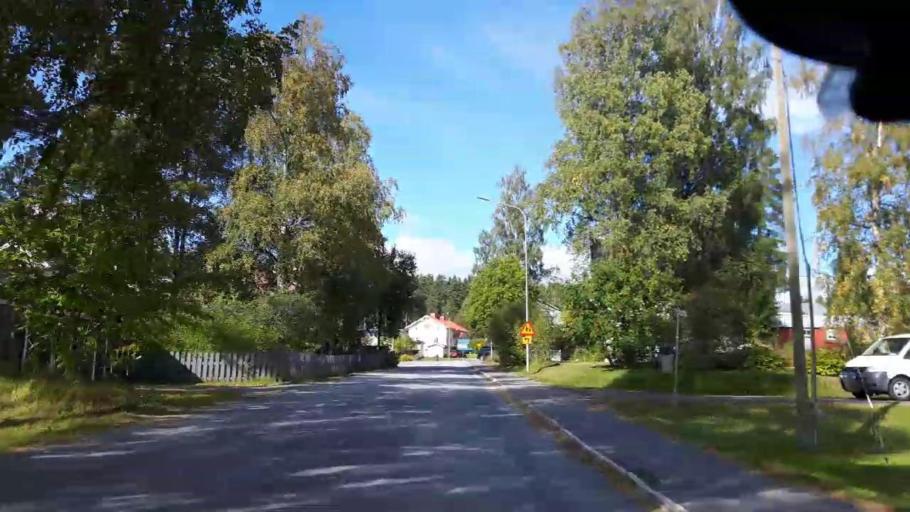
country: SE
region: Jaemtland
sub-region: Braecke Kommun
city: Braecke
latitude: 63.1662
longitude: 15.5987
